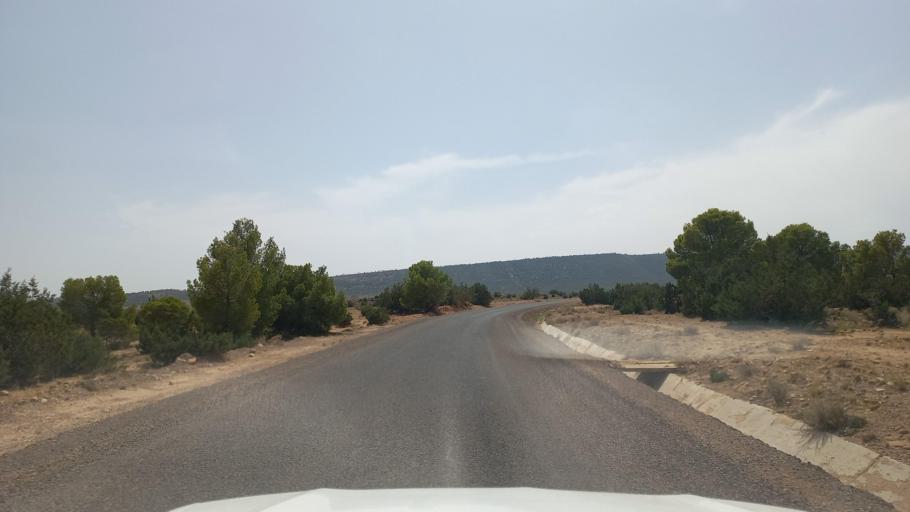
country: TN
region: Al Qasrayn
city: Sbiba
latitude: 35.3925
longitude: 8.9494
